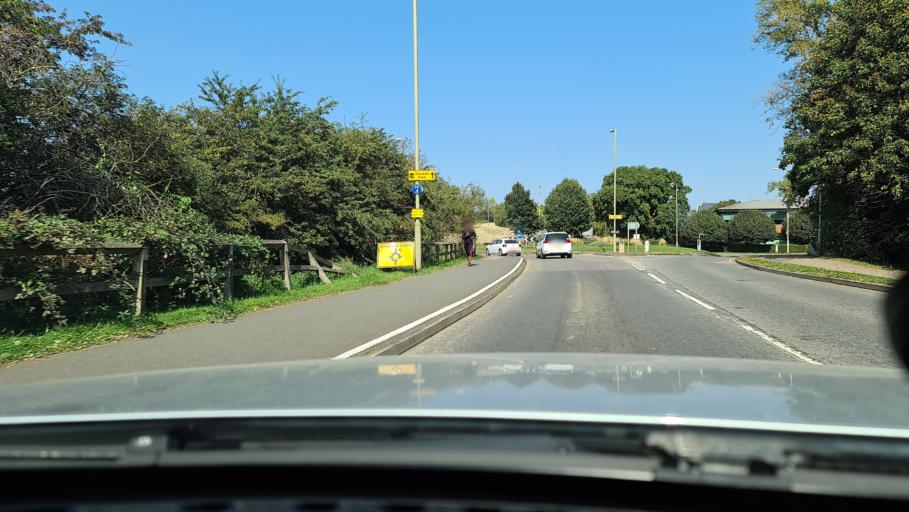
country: GB
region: England
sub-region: Oxfordshire
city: Banbury
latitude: 52.0812
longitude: -1.3364
